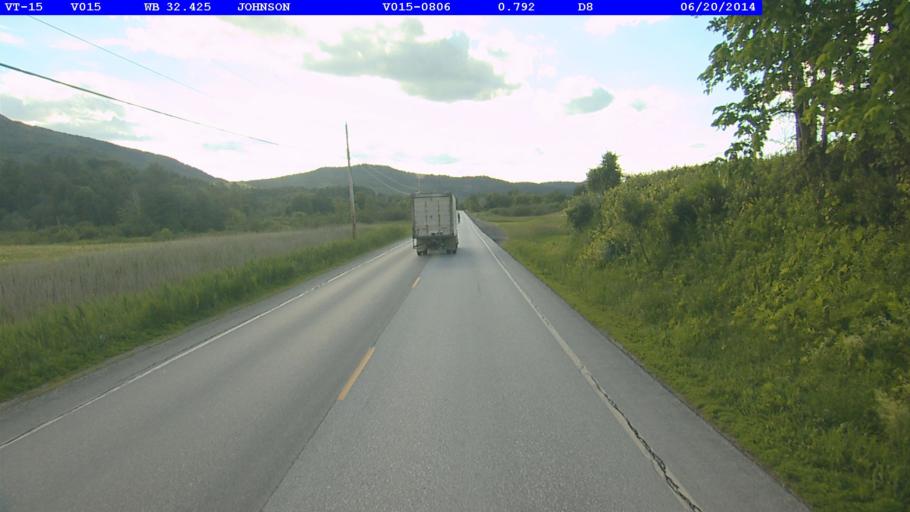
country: US
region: Vermont
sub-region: Lamoille County
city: Johnson
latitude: 44.6478
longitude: -72.7392
